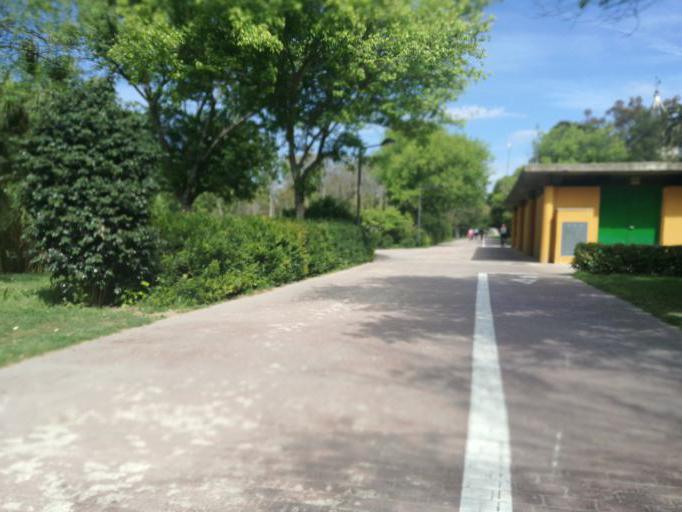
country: ES
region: Valencia
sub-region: Provincia de Valencia
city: Valencia
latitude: 39.4748
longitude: -0.3664
